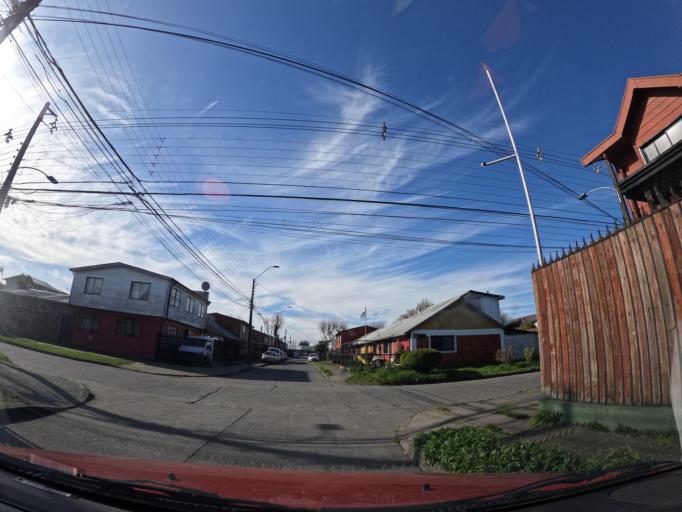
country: CL
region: Biobio
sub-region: Provincia de Concepcion
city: Concepcion
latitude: -36.8081
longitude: -73.0747
